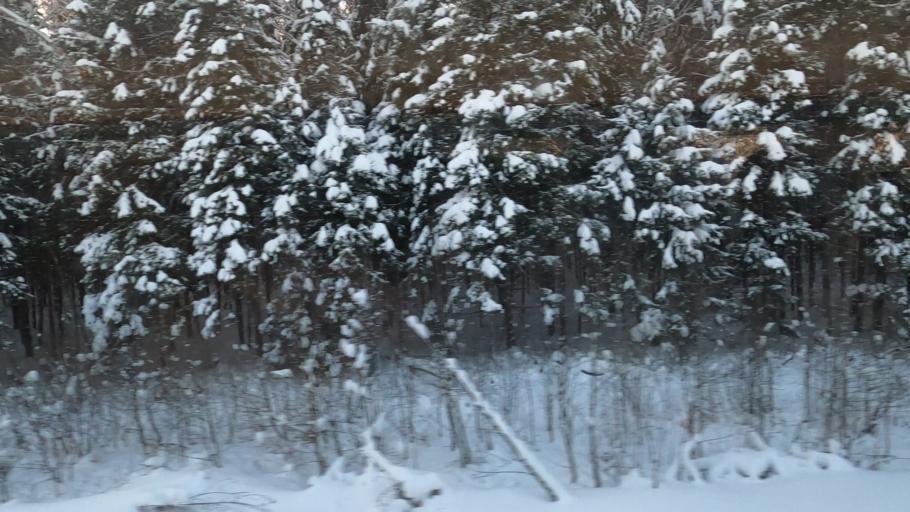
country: RU
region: Moskovskaya
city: Novo-Nikol'skoye
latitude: 56.5993
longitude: 37.5669
